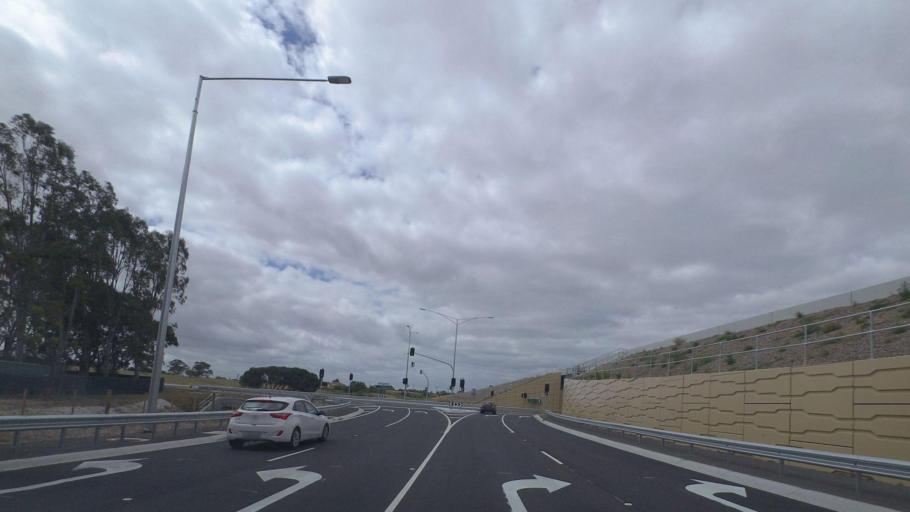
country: AU
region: Victoria
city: Heatherton
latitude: -37.9733
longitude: 145.1156
